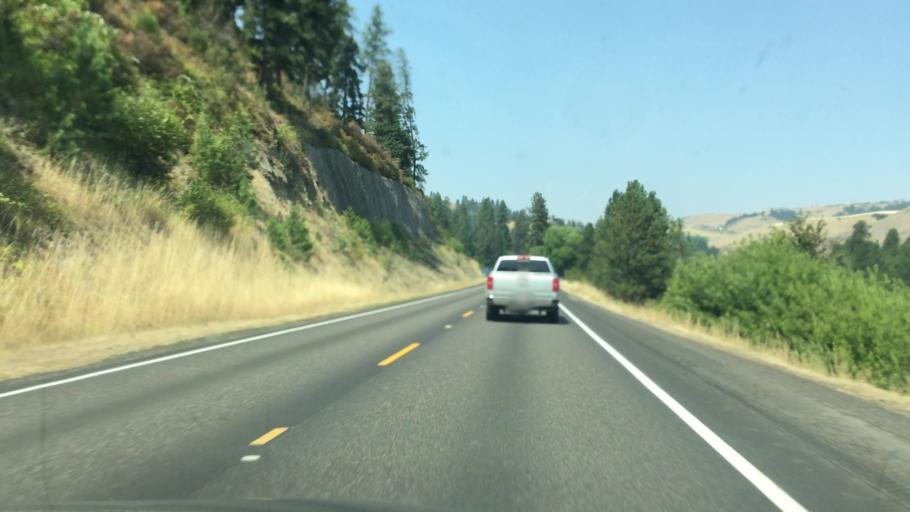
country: US
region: Idaho
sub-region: Clearwater County
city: Orofino
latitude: 46.4992
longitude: -116.4937
